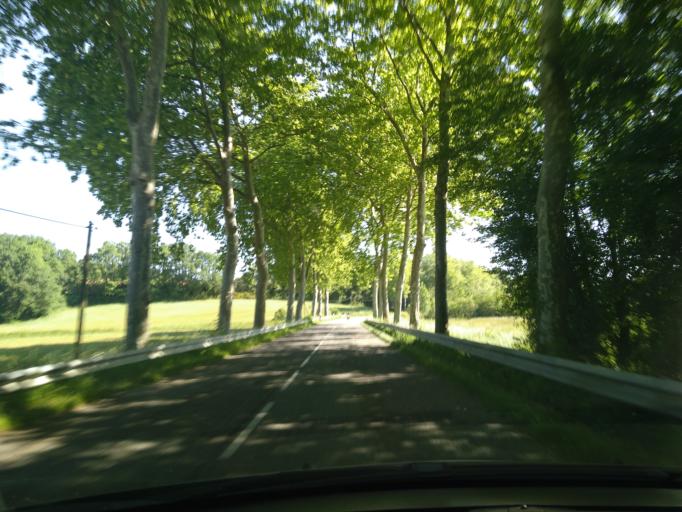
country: FR
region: Midi-Pyrenees
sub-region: Departement du Gers
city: Aubiet
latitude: 43.5362
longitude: 0.7708
